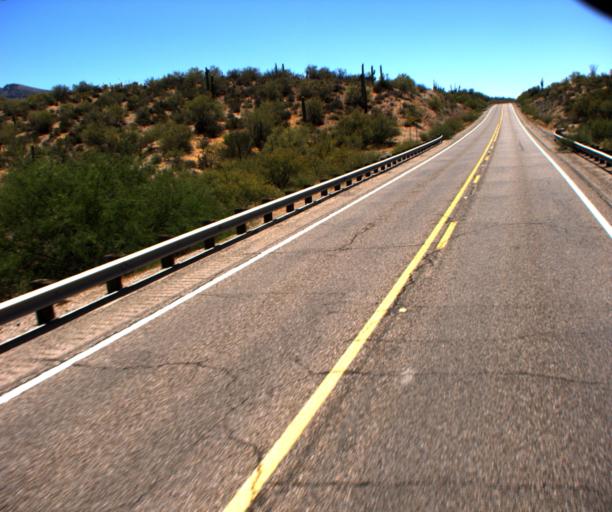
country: US
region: Arizona
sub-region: Pinal County
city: Kearny
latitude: 33.1092
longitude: -110.9515
